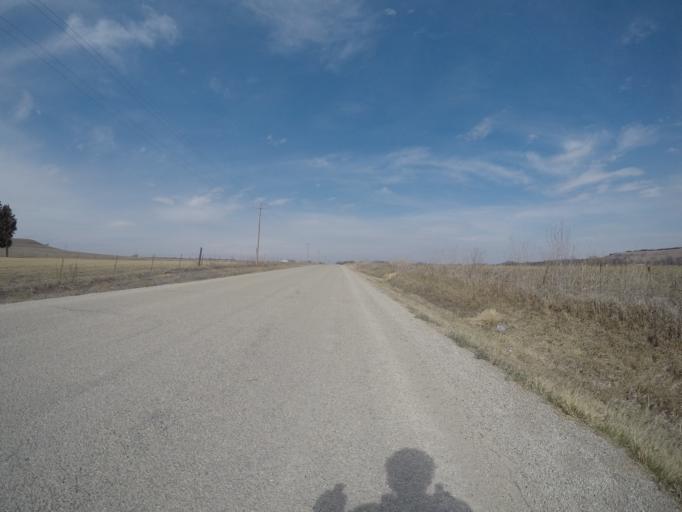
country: US
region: Kansas
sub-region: Geary County
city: Grandview Plaza
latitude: 39.0326
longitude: -96.7430
